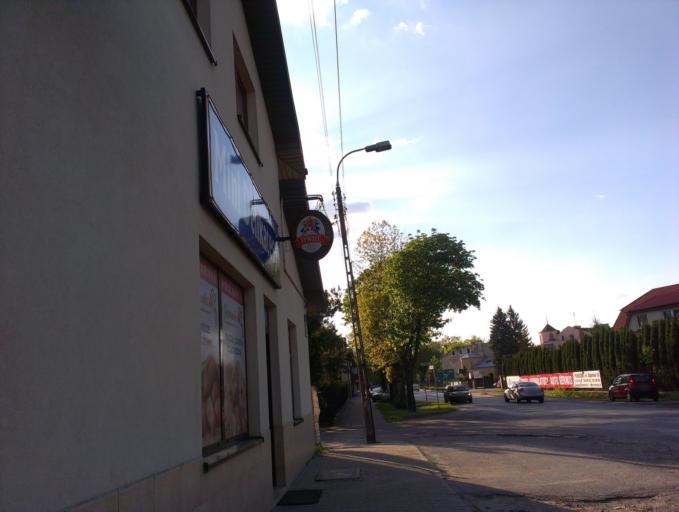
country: PL
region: Masovian Voivodeship
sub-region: Powiat piaseczynski
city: Piaseczno
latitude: 52.0663
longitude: 21.0305
